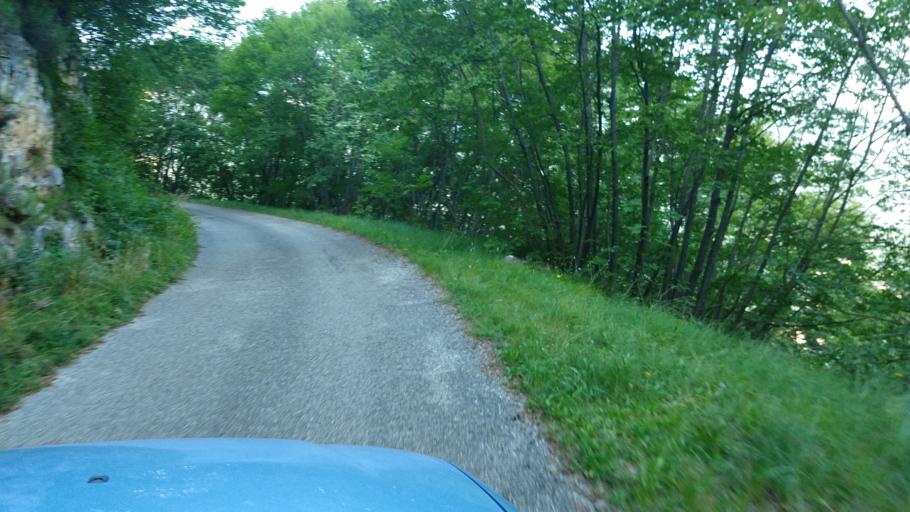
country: IT
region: Veneto
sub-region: Provincia di Vicenza
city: Campolongo sul Brenta
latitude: 45.8268
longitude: 11.6884
